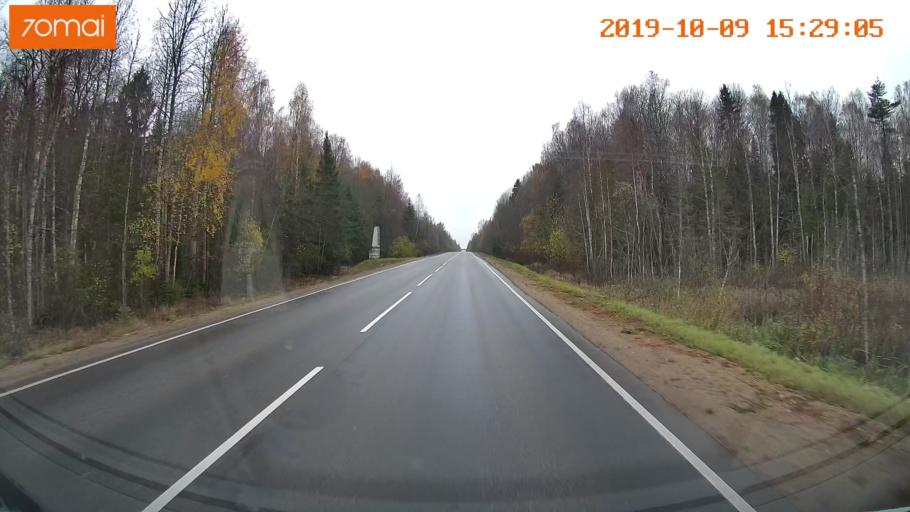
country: RU
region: Kostroma
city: Susanino
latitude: 57.9956
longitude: 41.3489
